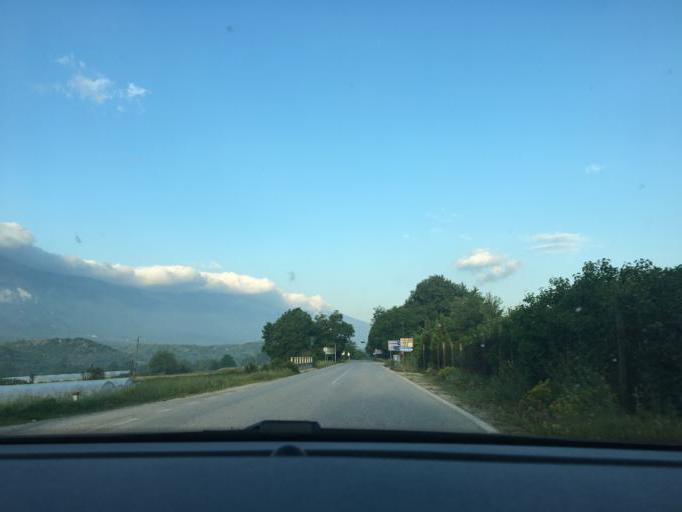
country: BG
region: Blagoevgrad
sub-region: Obshtina Petrich
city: Petrich
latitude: 41.3958
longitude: 23.0491
